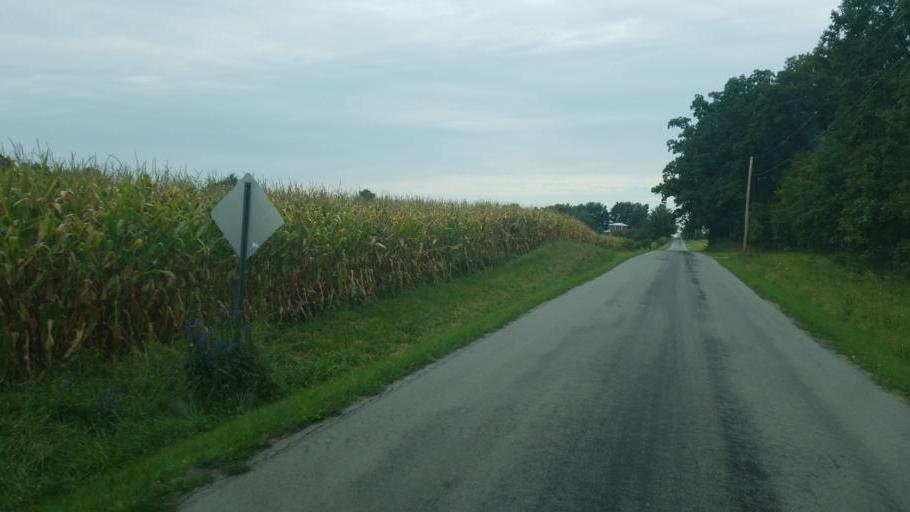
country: US
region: Ohio
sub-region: Wyandot County
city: Upper Sandusky
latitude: 40.8279
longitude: -83.1888
